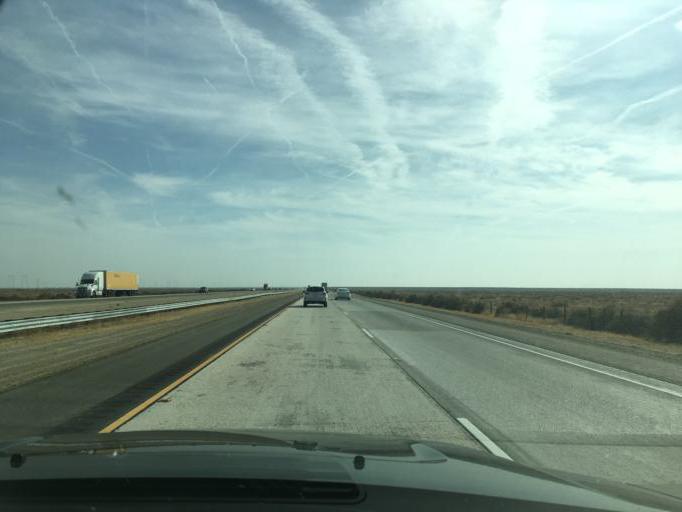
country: US
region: California
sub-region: Kern County
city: Lost Hills
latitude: 35.5526
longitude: -119.5923
